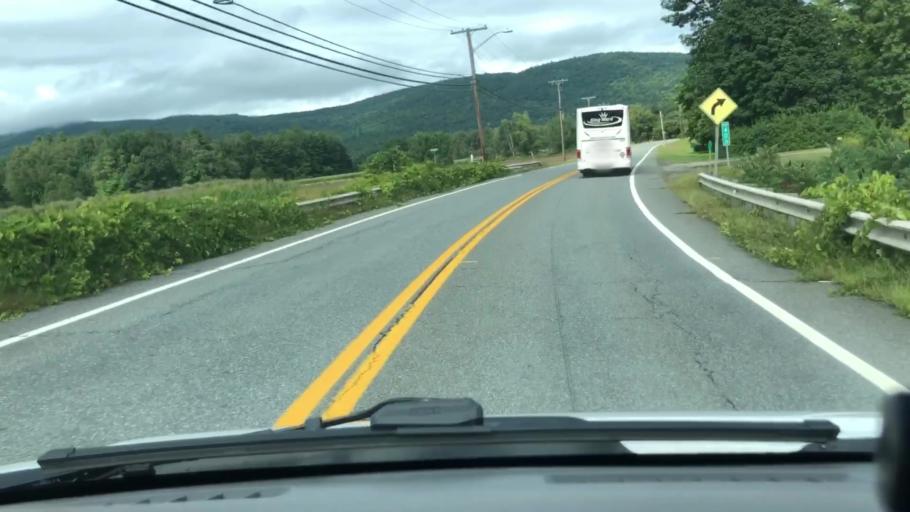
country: US
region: Massachusetts
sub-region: Franklin County
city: Buckland
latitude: 42.6095
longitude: -72.7747
